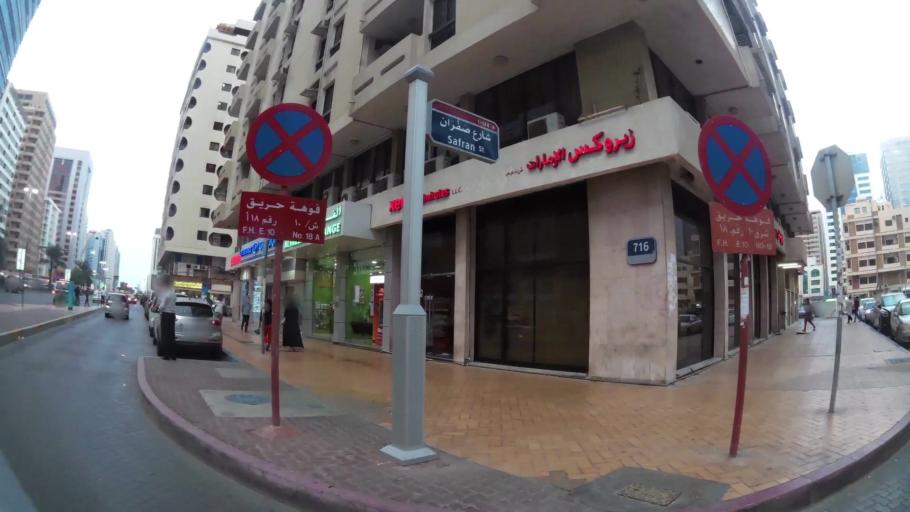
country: AE
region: Abu Dhabi
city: Abu Dhabi
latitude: 24.4943
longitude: 54.3702
